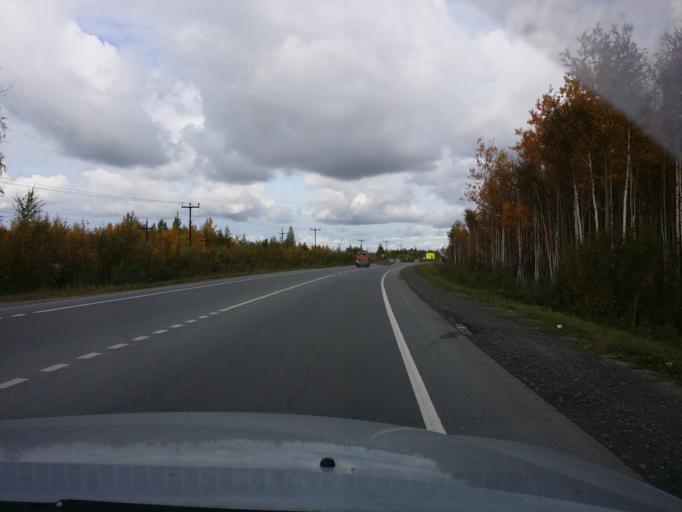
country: RU
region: Khanty-Mansiyskiy Avtonomnyy Okrug
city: Nizhnevartovsk
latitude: 61.0273
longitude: 76.3653
